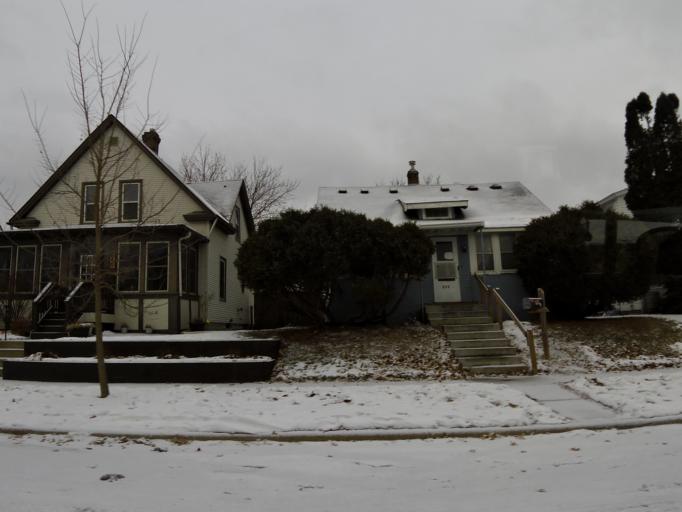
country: US
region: Minnesota
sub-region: Dakota County
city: West Saint Paul
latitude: 44.9224
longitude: -93.1398
